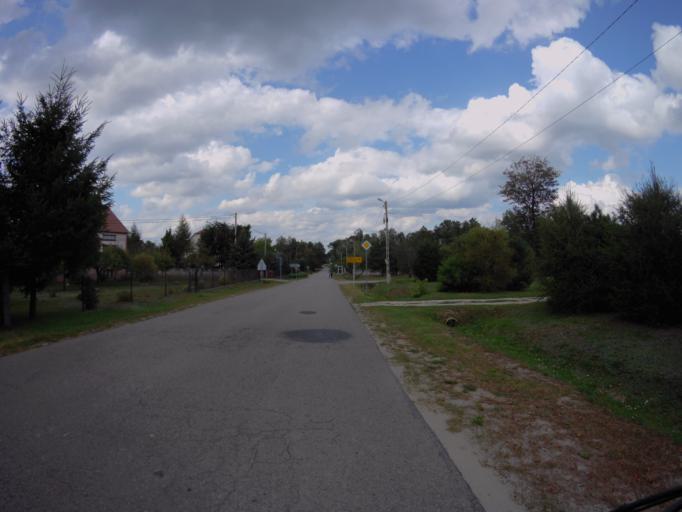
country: PL
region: Subcarpathian Voivodeship
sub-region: Powiat lezajski
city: Brzoza Krolewska
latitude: 50.2423
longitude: 22.3280
